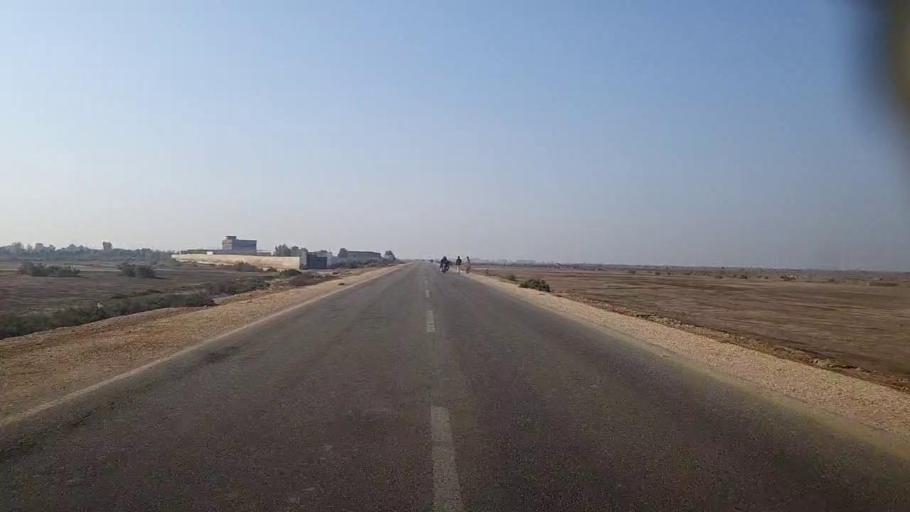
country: PK
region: Sindh
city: Gharo
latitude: 24.7014
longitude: 67.5282
